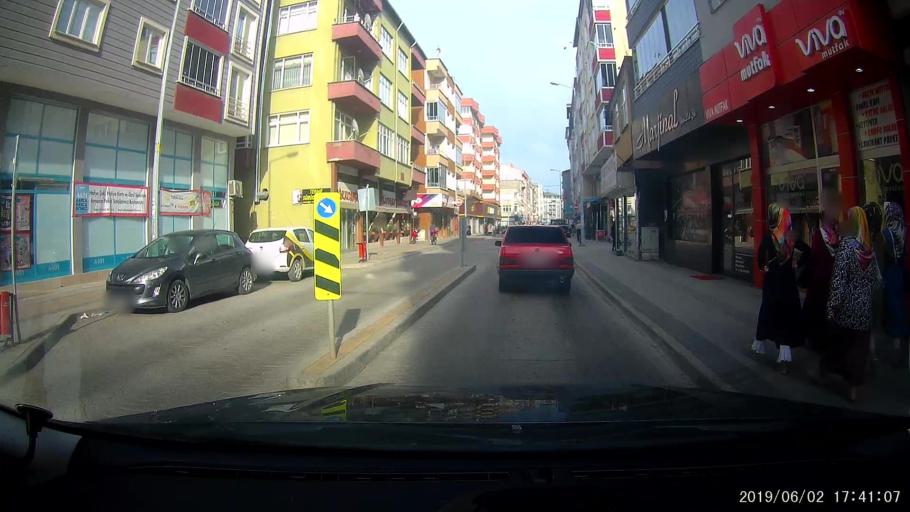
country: TR
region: Samsun
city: Terme
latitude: 41.2107
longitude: 36.9688
